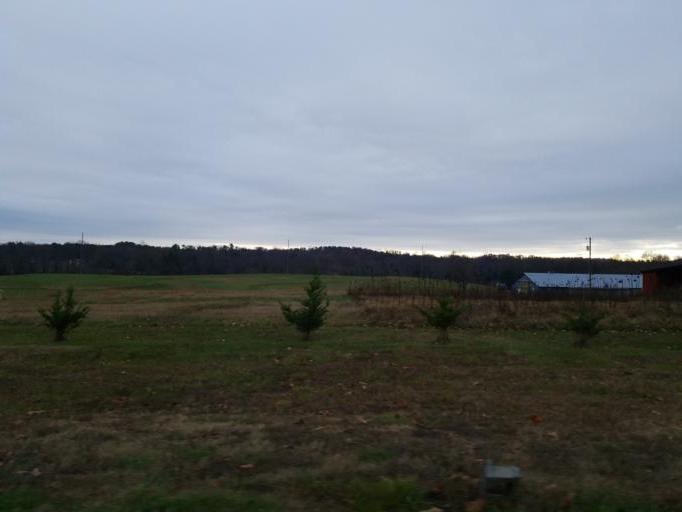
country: US
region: Georgia
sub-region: Dawson County
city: Dawsonville
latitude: 34.4882
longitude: -84.1748
